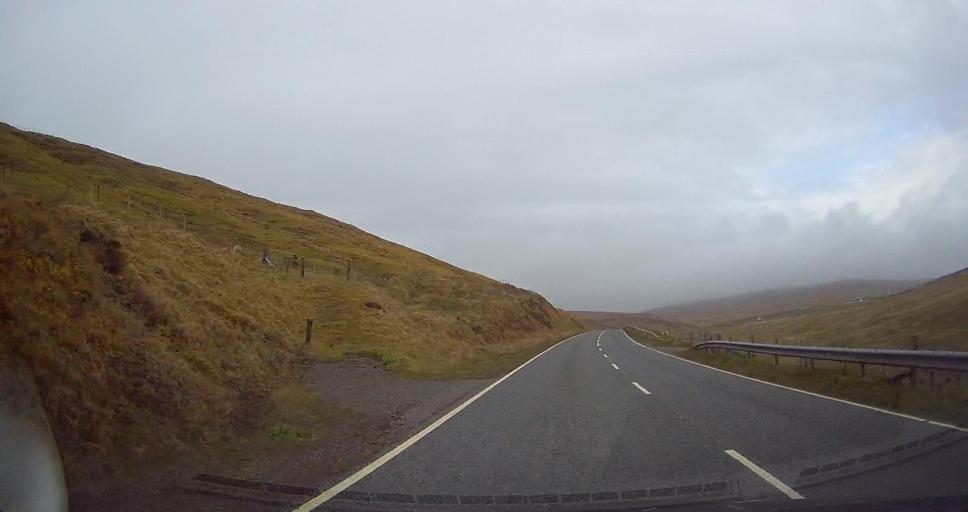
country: GB
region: Scotland
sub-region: Shetland Islands
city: Sandwick
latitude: 59.9976
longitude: -1.2791
